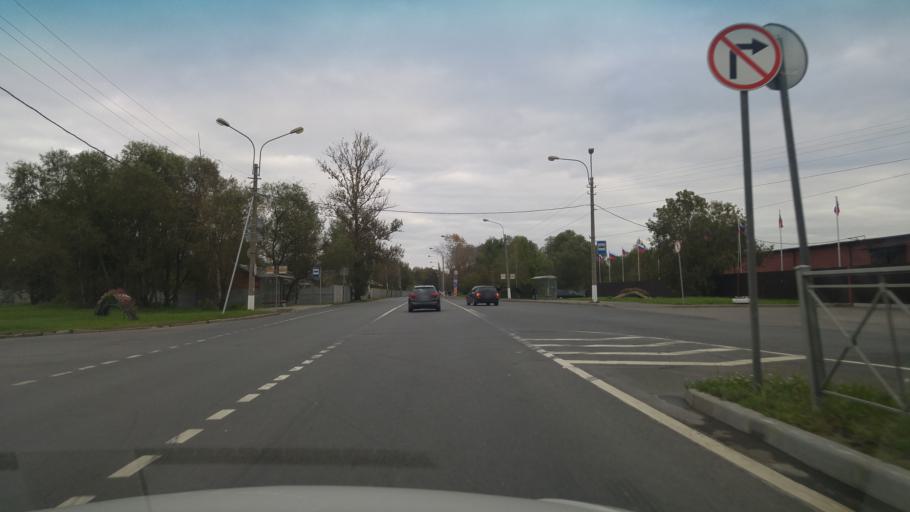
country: RU
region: St.-Petersburg
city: Kronshtadt
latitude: 60.0068
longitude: 29.7411
